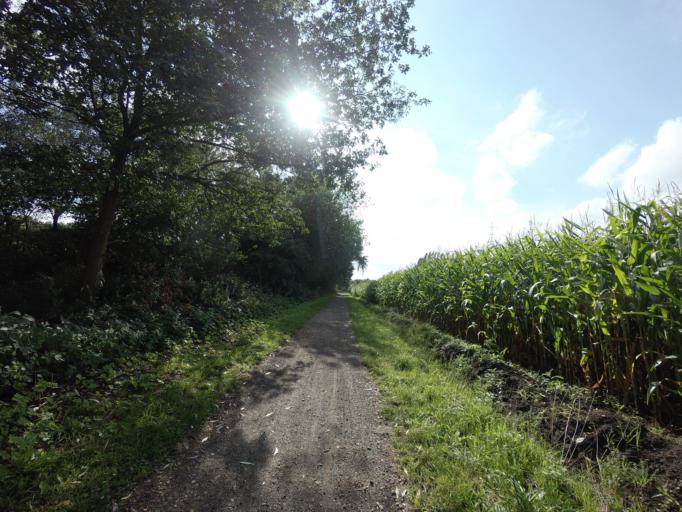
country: BE
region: Flanders
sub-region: Provincie Antwerpen
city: Aartselaar
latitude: 51.1144
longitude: 4.3992
